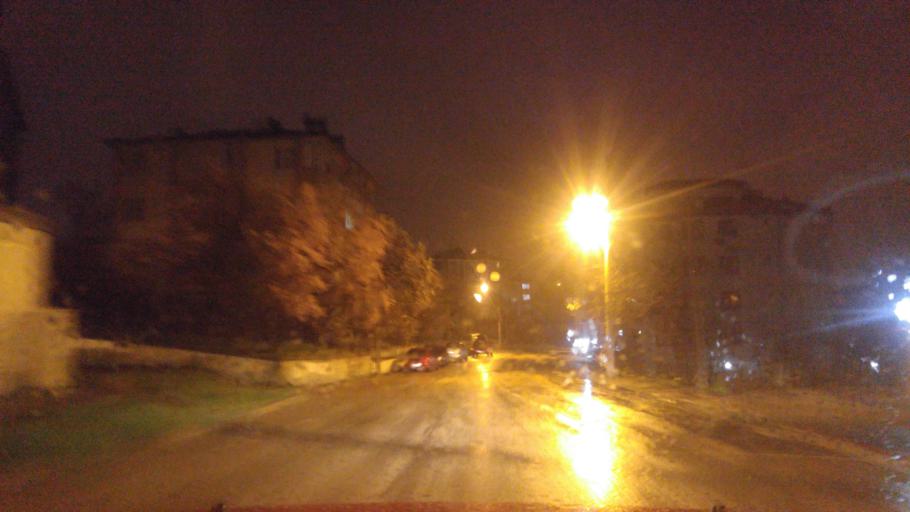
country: TR
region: Karabuk
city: Safranbolu
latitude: 41.2506
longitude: 32.6721
